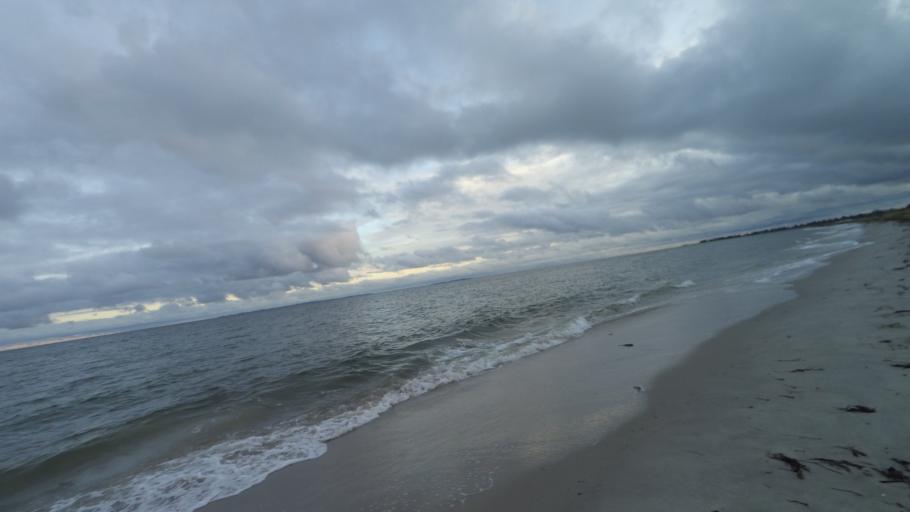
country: DK
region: Central Jutland
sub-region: Arhus Kommune
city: Beder
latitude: 56.0453
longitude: 10.2711
